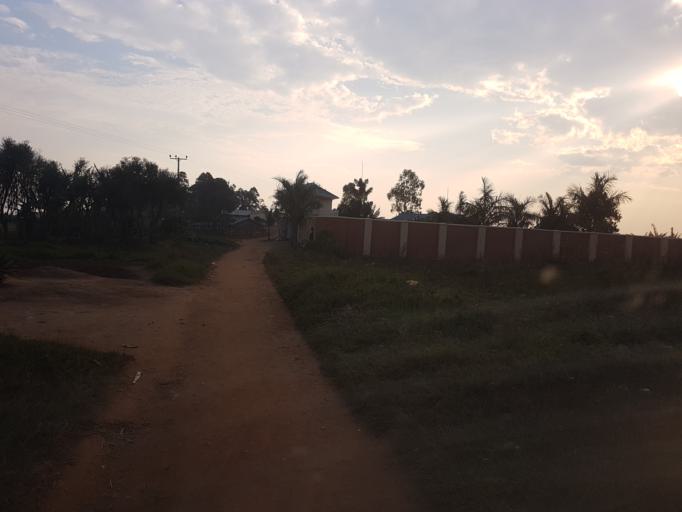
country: UG
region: Western Region
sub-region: Rukungiri District
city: Rukungiri
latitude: -0.7633
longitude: 29.9282
